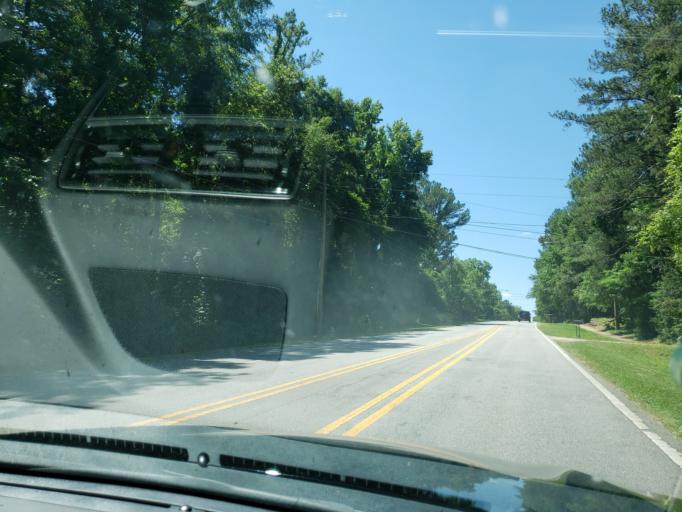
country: US
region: Alabama
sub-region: Lee County
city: Auburn
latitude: 32.6270
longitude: -85.4820
